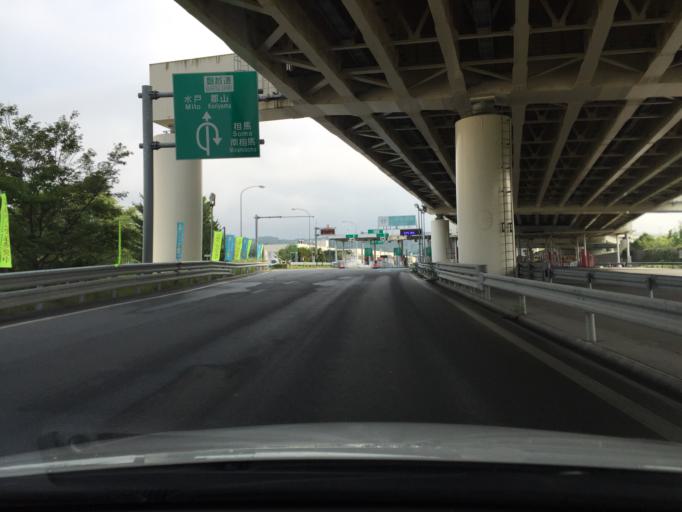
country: JP
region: Fukushima
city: Iwaki
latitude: 37.0687
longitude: 140.8394
